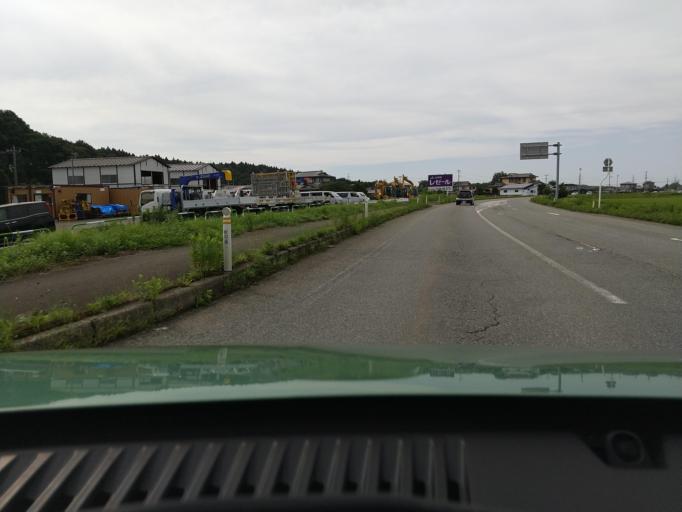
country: JP
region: Akita
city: Akita Shi
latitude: 39.7951
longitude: 140.0974
